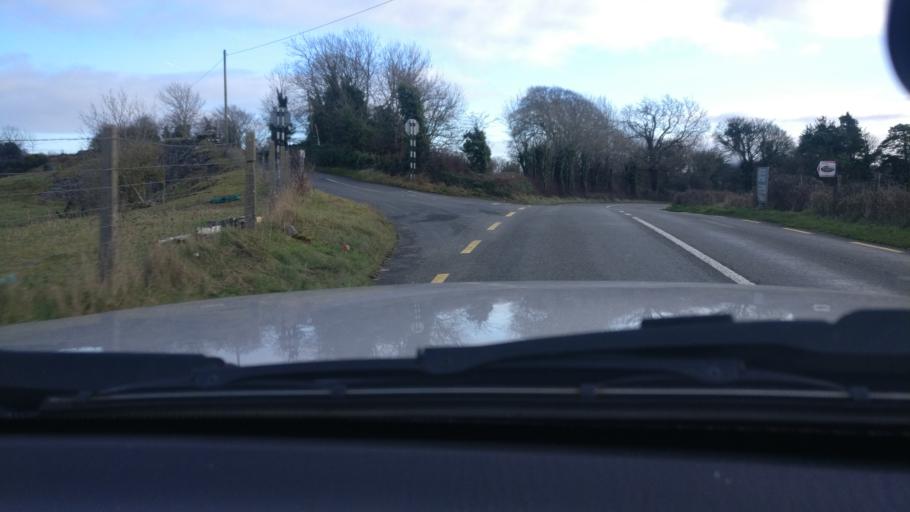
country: IE
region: Connaught
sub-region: County Galway
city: Ballinasloe
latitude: 53.2937
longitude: -8.2413
